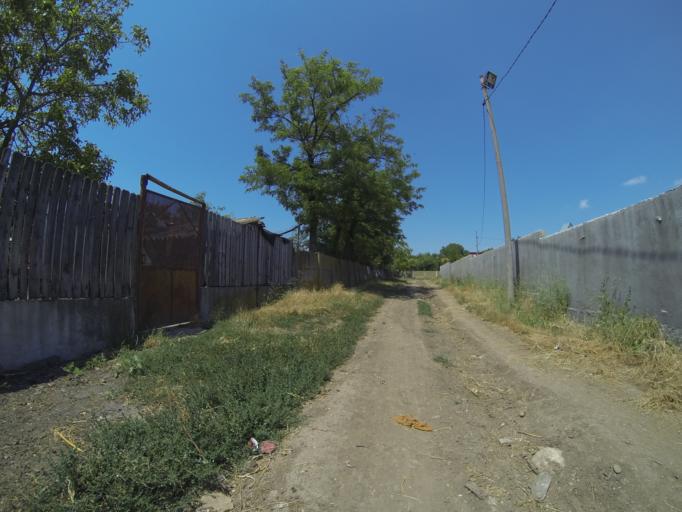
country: RO
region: Dolj
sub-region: Comuna Segarcea
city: Segarcea
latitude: 44.0913
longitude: 23.7537
